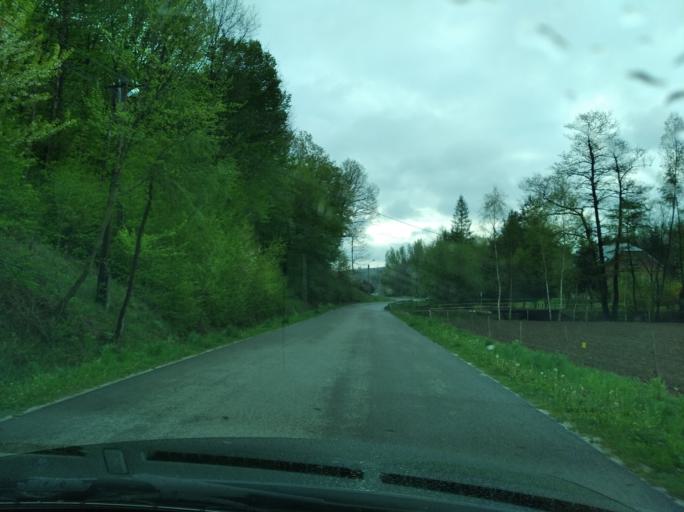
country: PL
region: Subcarpathian Voivodeship
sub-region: Powiat rzeszowski
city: Lecka
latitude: 49.8750
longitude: 22.0200
